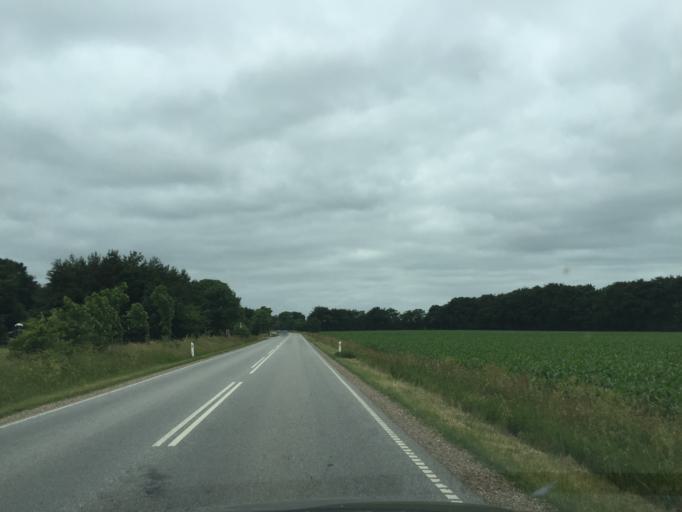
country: DK
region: South Denmark
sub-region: Esbjerg Kommune
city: Ribe
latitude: 55.3879
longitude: 8.8708
